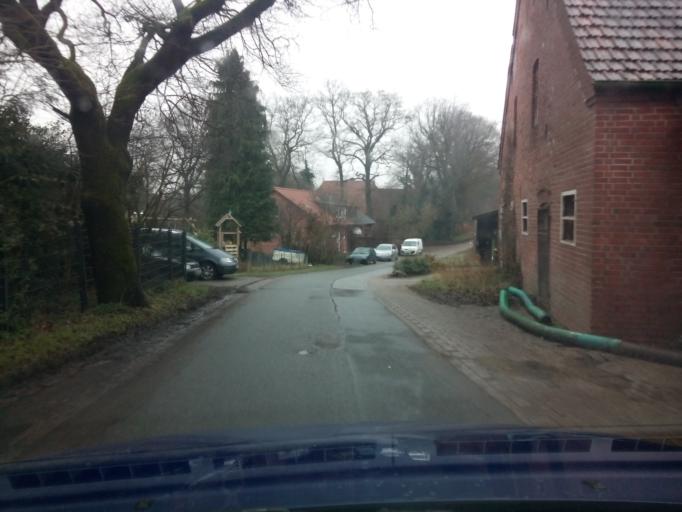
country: DE
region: Lower Saxony
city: Osterholz-Scharmbeck
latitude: 53.2457
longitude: 8.7994
